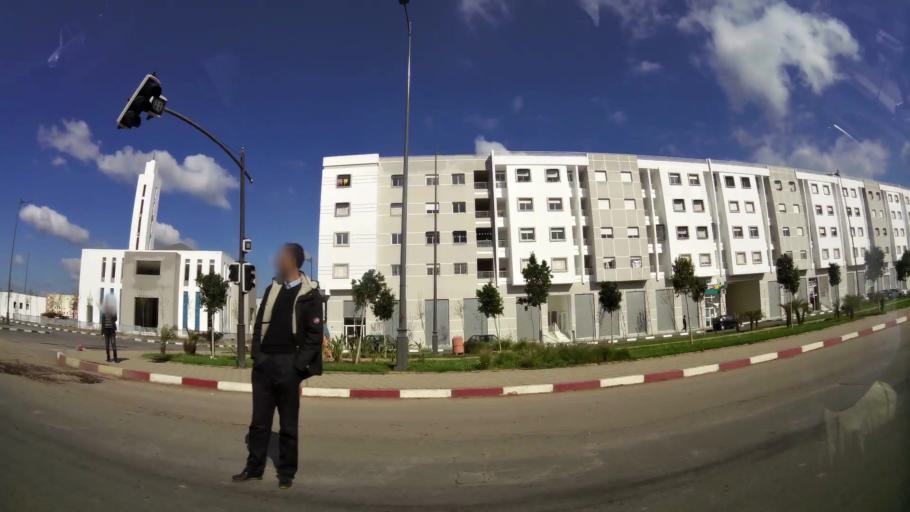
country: MA
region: Chaouia-Ouardigha
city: Nouaseur
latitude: 33.3712
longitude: -7.5425
